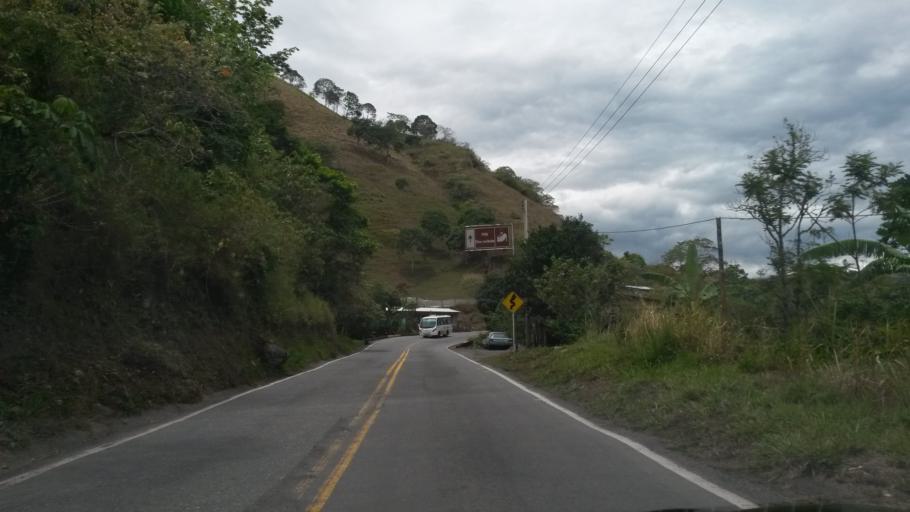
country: CO
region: Cauca
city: Rosas
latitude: 2.2535
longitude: -76.7618
